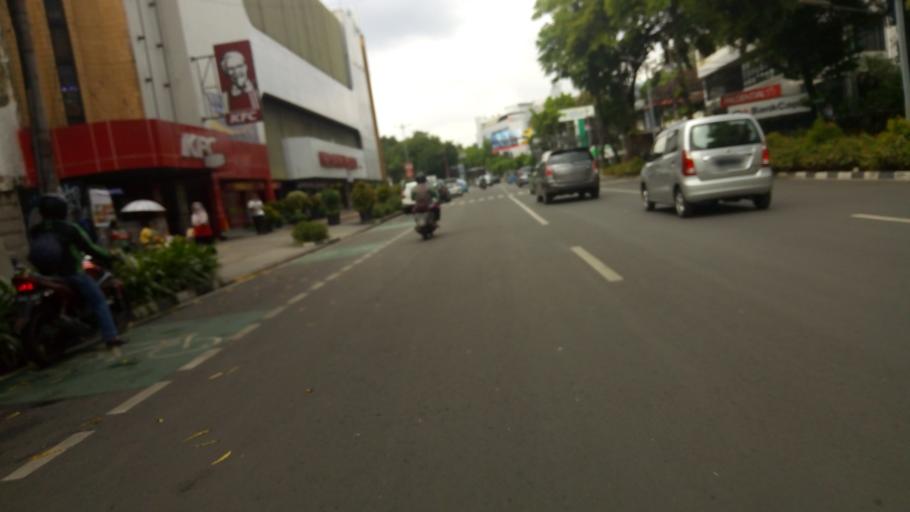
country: ID
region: Jakarta Raya
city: Jakarta
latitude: -6.2459
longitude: 106.8019
